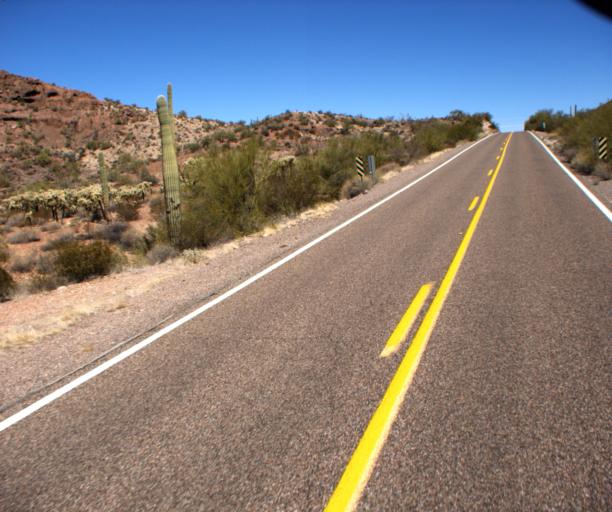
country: MX
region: Sonora
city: Sonoyta
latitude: 32.0819
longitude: -112.7786
